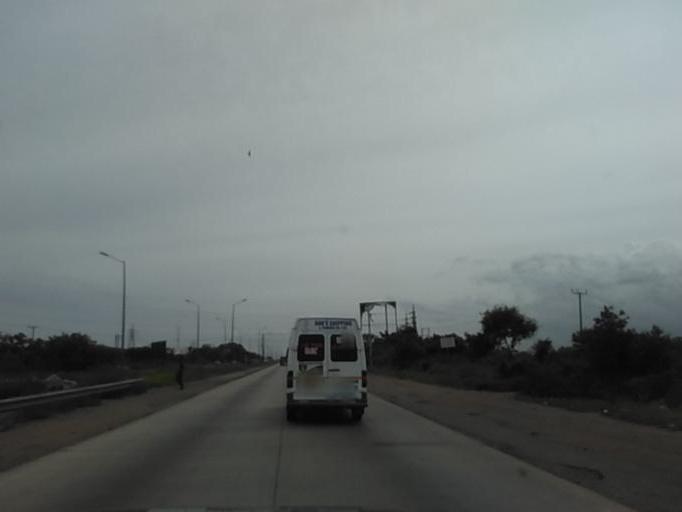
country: GH
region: Greater Accra
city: Nungua
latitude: 5.6503
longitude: -0.1056
